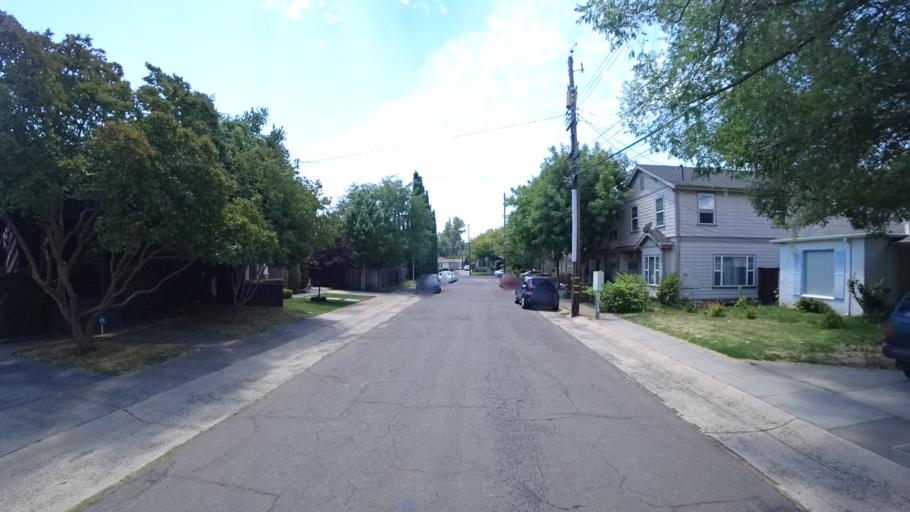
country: US
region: California
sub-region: Sacramento County
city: Sacramento
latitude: 38.5669
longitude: -121.4406
